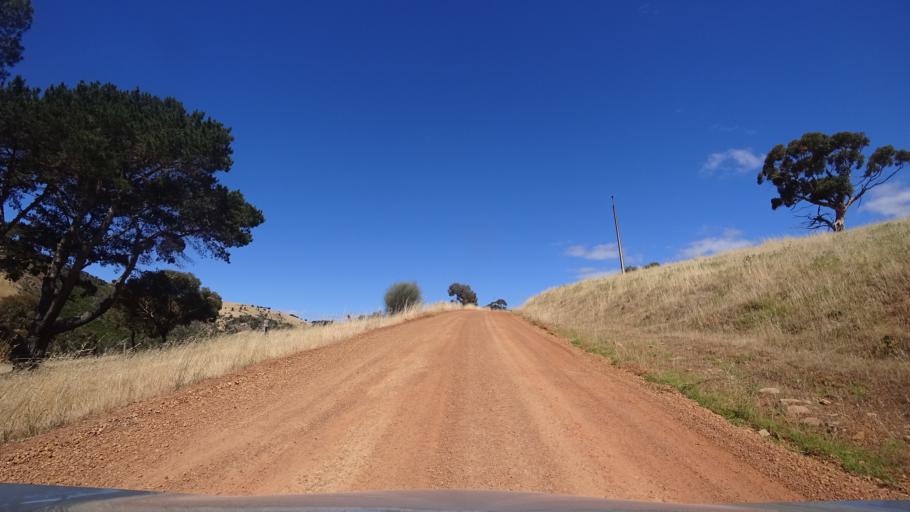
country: AU
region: South Australia
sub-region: Kangaroo Island
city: Kingscote
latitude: -35.6821
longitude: 136.9725
